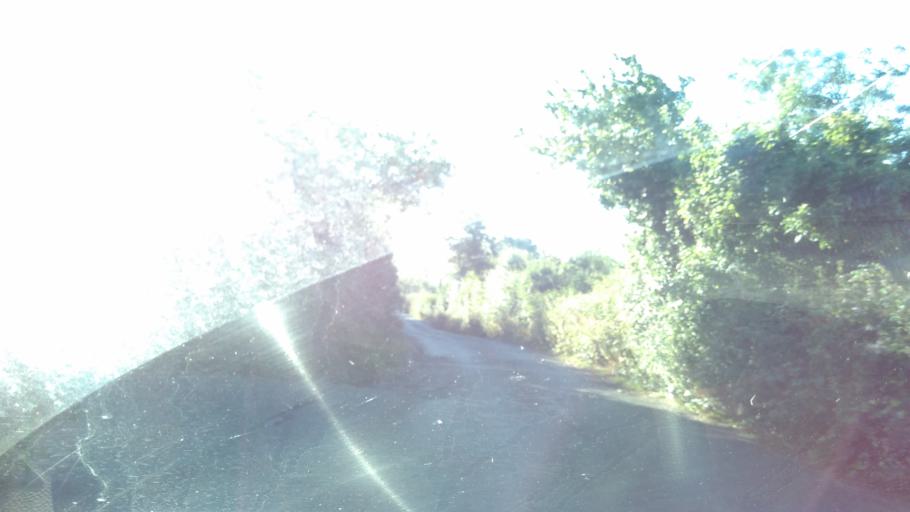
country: GB
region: England
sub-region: Kent
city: Blean
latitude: 51.3156
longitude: 1.0196
